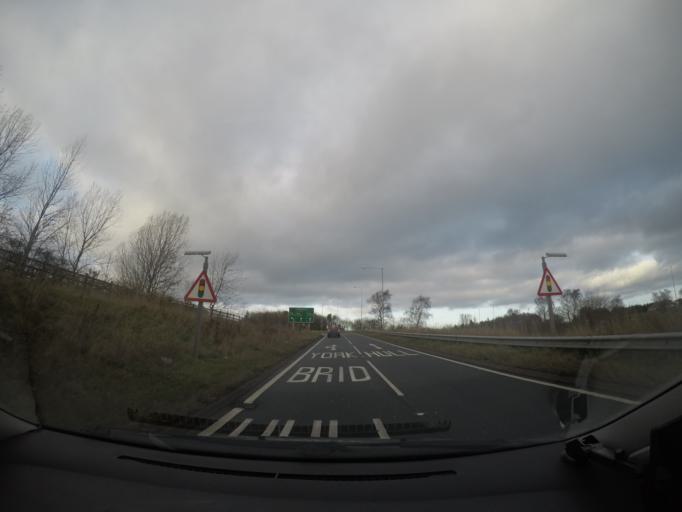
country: GB
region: England
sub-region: City of York
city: Murton
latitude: 53.9550
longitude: -1.0122
